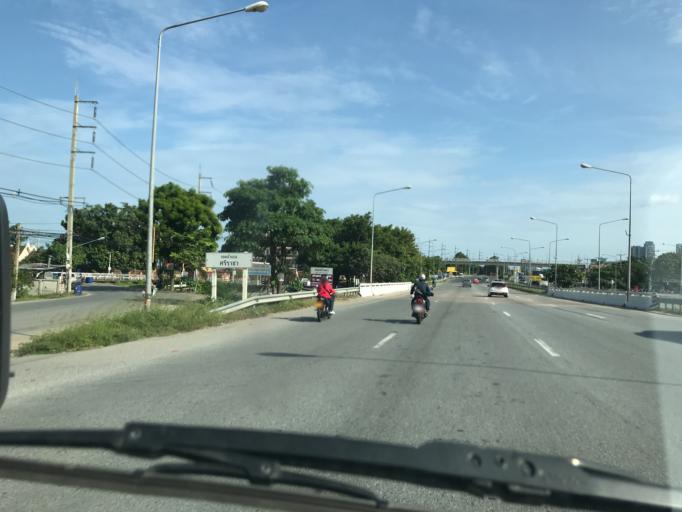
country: TH
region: Chon Buri
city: Bang Lamung
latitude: 13.0689
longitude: 100.9239
